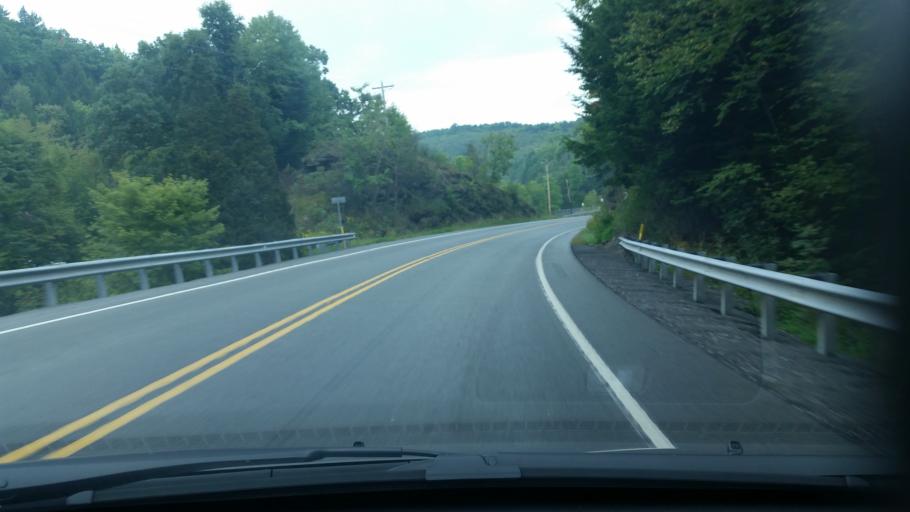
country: US
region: Pennsylvania
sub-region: Clearfield County
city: Shiloh
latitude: 41.0886
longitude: -78.2450
